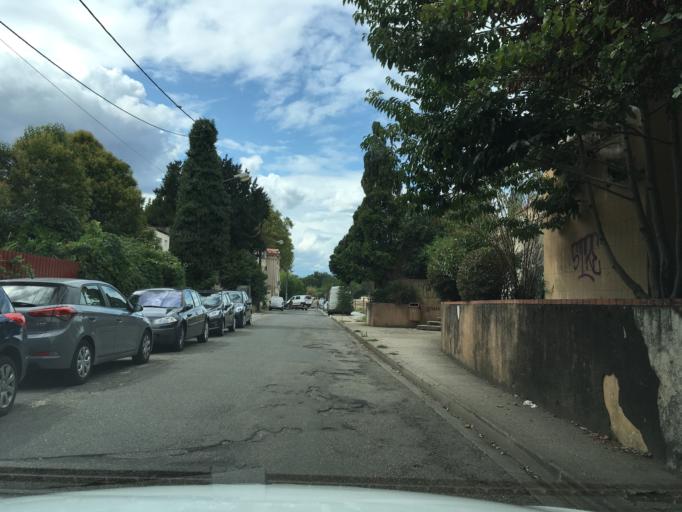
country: FR
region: Aquitaine
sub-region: Departement du Lot-et-Garonne
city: Le Passage
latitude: 44.2071
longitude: 0.6107
